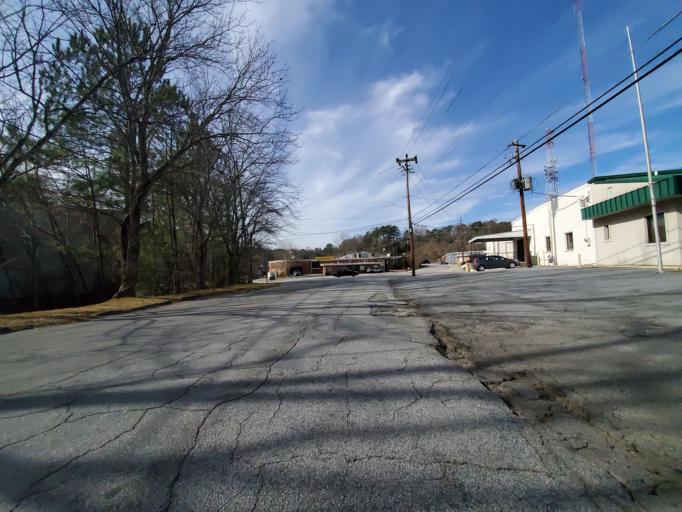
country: US
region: Georgia
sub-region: DeKalb County
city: Druid Hills
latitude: 33.8054
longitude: -84.3401
